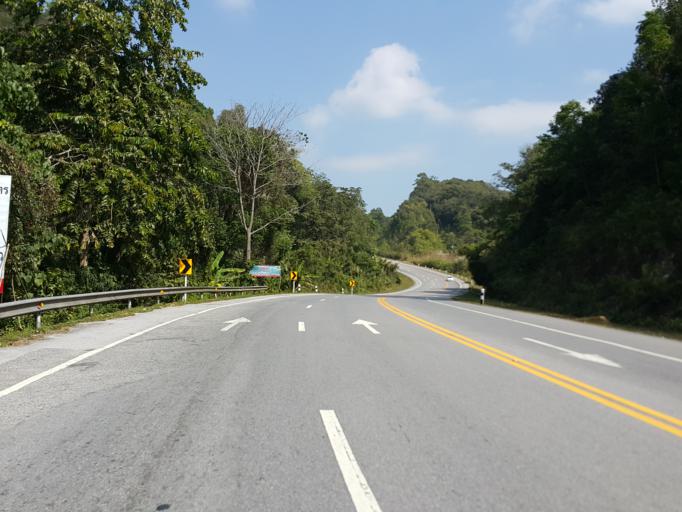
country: TH
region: Lampang
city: Wang Nuea
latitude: 19.0644
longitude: 99.3723
